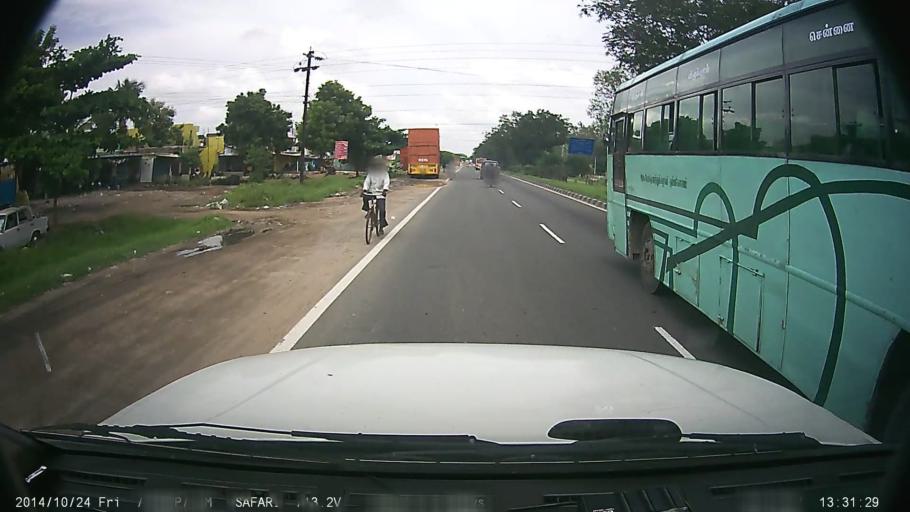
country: IN
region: Tamil Nadu
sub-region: Kancheepuram
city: Singapperumalkovil
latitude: 12.7445
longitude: 79.9933
